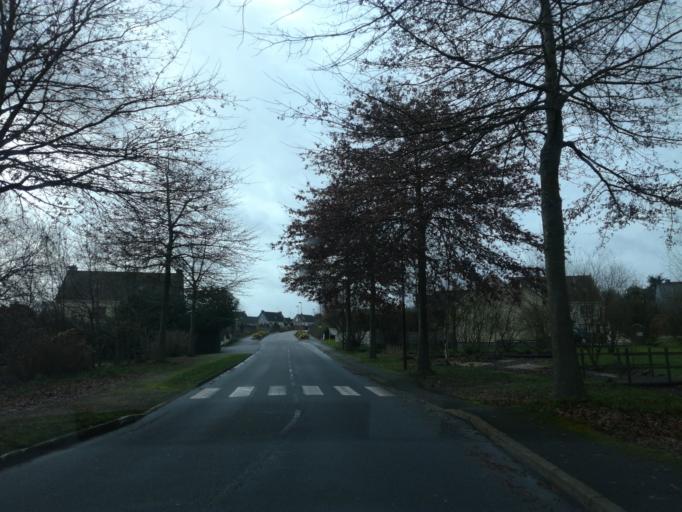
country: FR
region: Brittany
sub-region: Departement du Morbihan
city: Le Sourn
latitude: 48.0455
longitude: -2.9861
